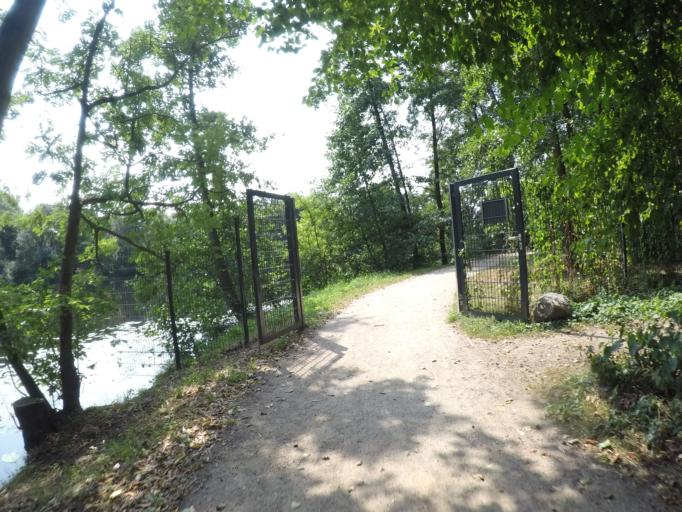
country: DE
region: Hamburg
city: Harburg
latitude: 53.4939
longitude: 9.9951
